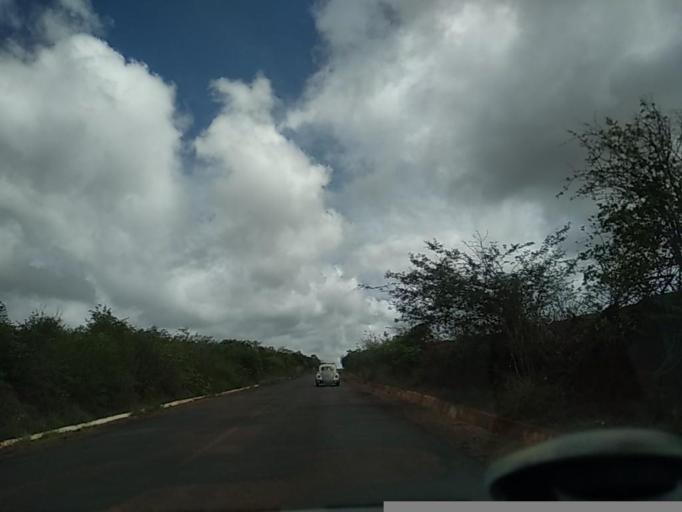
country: BR
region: Bahia
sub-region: Caetite
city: Caetite
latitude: -14.0402
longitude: -42.4862
